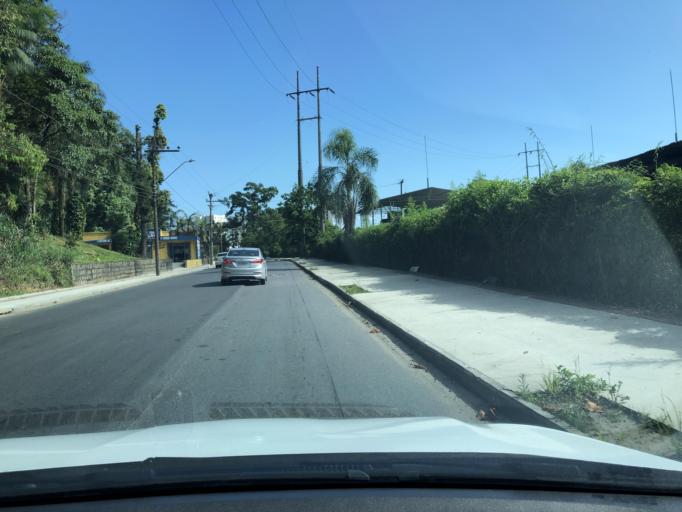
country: BR
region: Santa Catarina
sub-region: Joinville
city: Joinville
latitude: -26.3074
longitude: -48.8358
